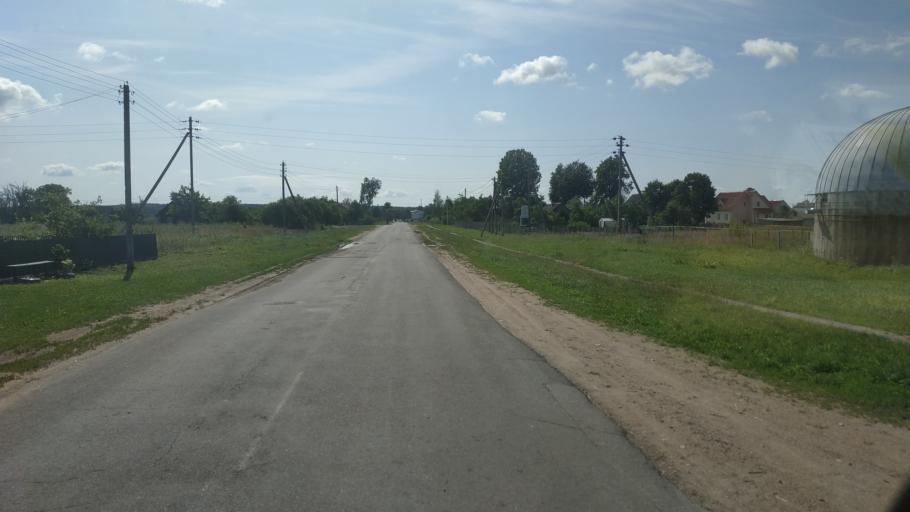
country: BY
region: Mogilev
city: Poselok Voskhod
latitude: 53.7090
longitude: 30.4998
